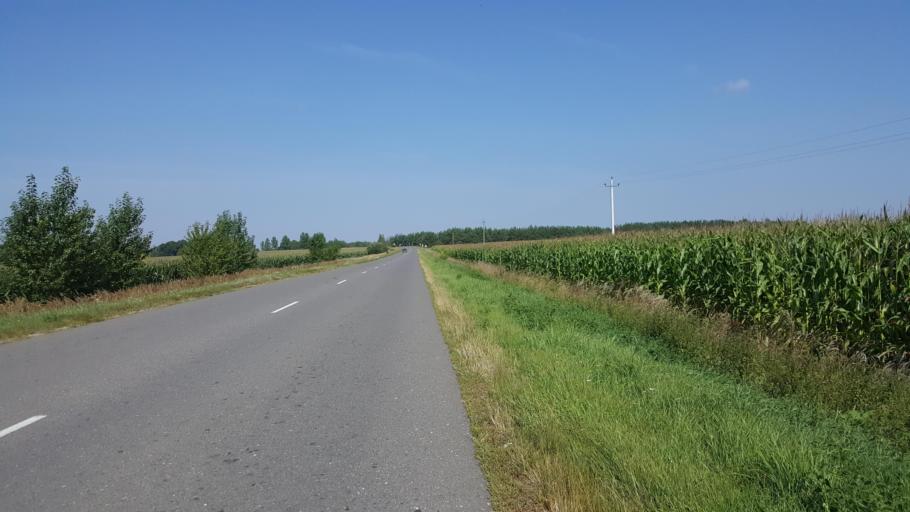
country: BY
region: Brest
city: Kamyanyuki
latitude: 52.4862
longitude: 23.6948
